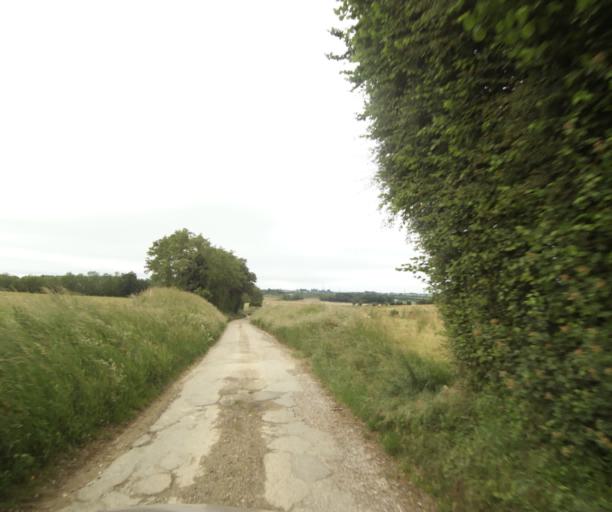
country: FR
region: Rhone-Alpes
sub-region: Departement de l'Ain
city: Miribel
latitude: 45.8479
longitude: 4.9447
